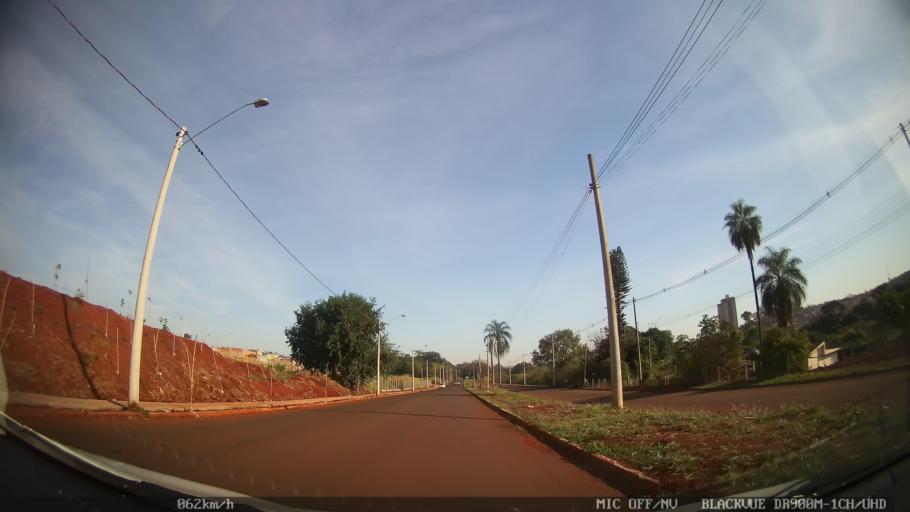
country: BR
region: Sao Paulo
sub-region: Ribeirao Preto
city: Ribeirao Preto
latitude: -21.2752
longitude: -47.8092
